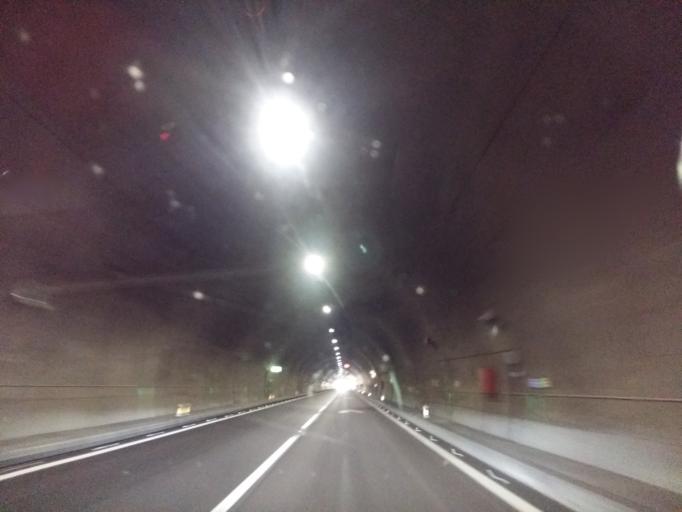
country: PT
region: Castelo Branco
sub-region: Concelho do Fundao
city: Fundao
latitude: 40.1119
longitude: -7.4730
